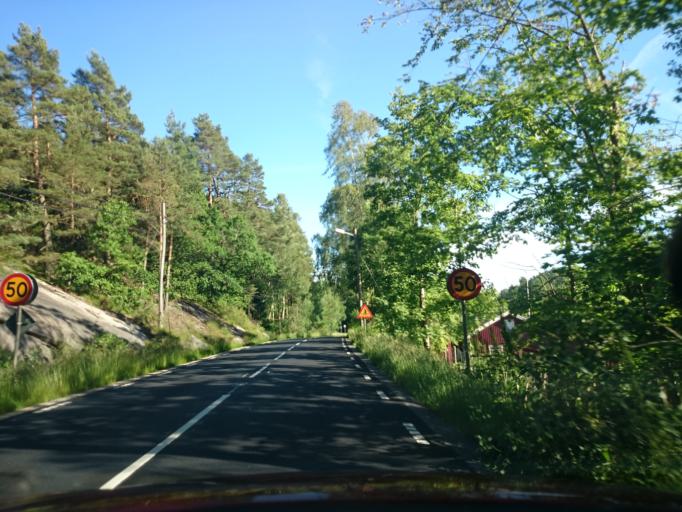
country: SE
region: Vaestra Goetaland
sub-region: Lerums Kommun
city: Lerum
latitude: 57.7797
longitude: 12.2540
